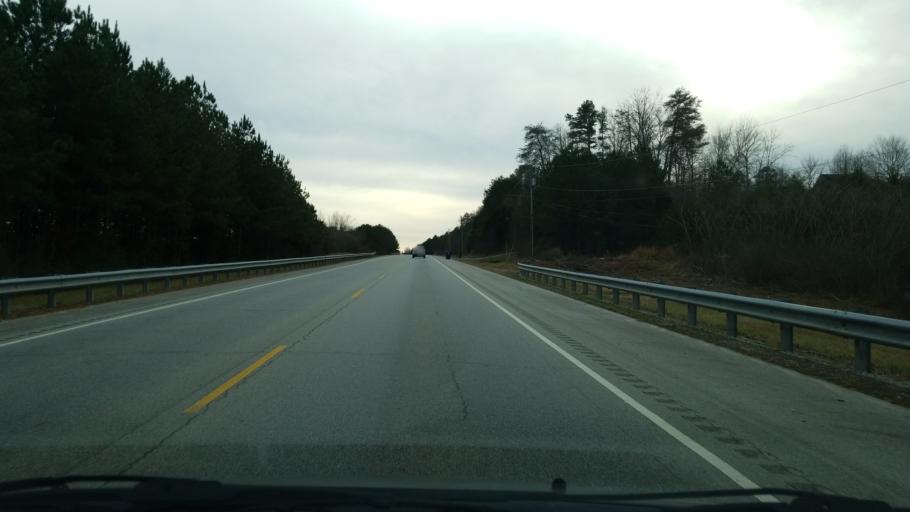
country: US
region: Tennessee
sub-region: Hamilton County
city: Collegedale
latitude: 35.0783
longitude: -85.0708
